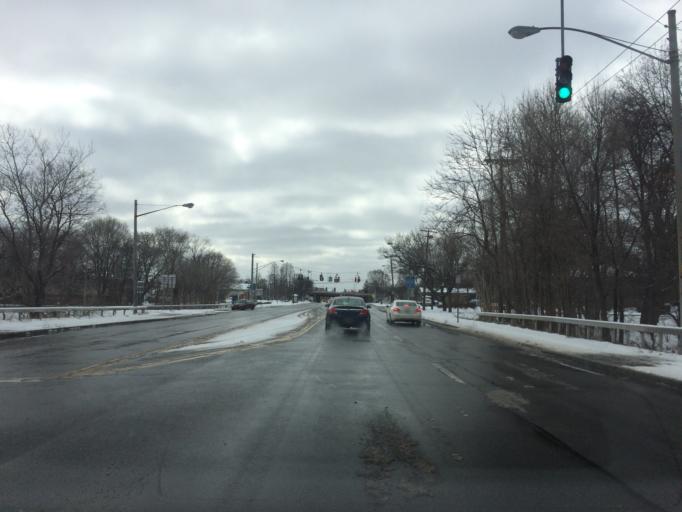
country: US
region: New York
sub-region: Monroe County
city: Brighton
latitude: 43.1175
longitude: -77.5547
